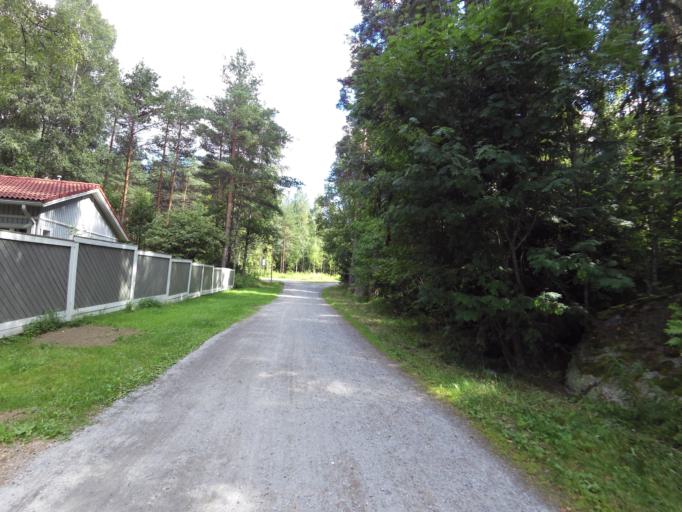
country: FI
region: Pirkanmaa
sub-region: Tampere
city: Yloejaervi
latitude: 61.5117
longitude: 23.6105
